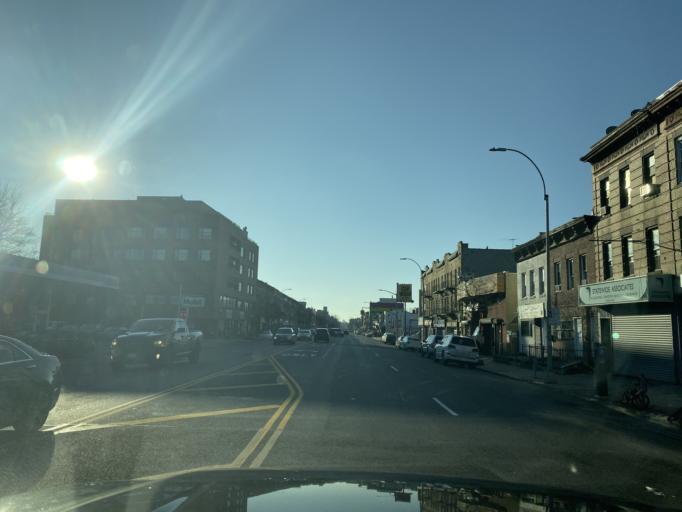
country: US
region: New York
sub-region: Kings County
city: Brooklyn
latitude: 40.6423
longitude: -73.9697
